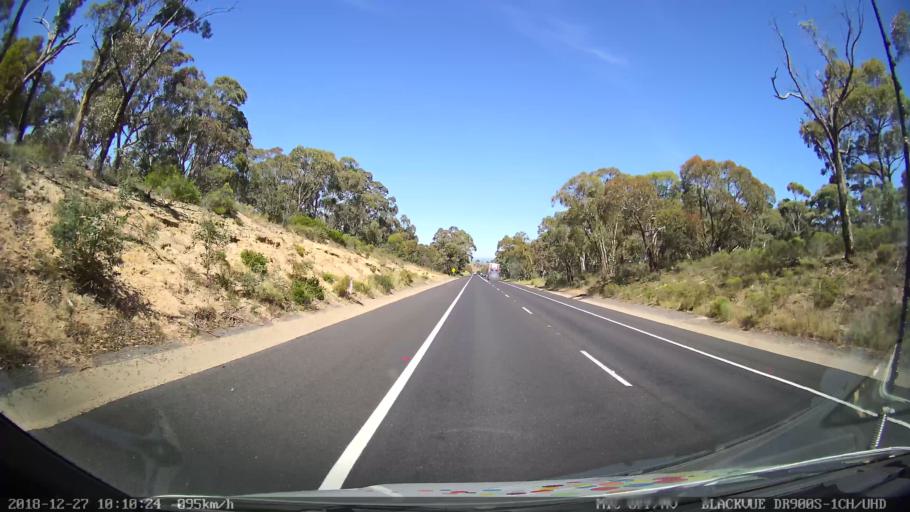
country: AU
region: New South Wales
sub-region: Bathurst Regional
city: Kelso
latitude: -33.4522
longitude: 149.7925
